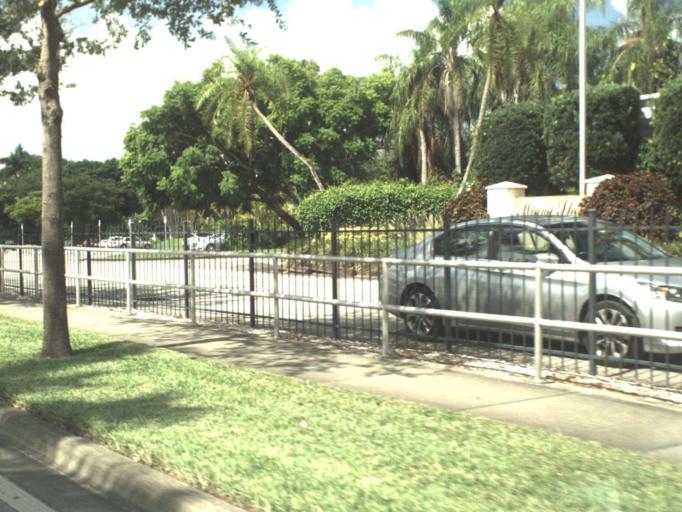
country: US
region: Florida
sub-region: Miami-Dade County
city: Biscayne Park
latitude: 25.8681
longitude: -80.1759
